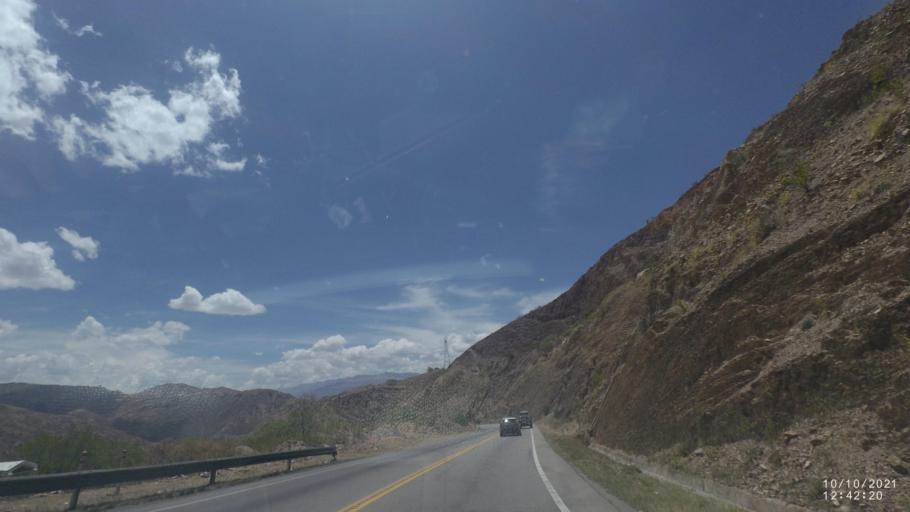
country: BO
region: Cochabamba
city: Irpa Irpa
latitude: -17.6305
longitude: -66.3923
